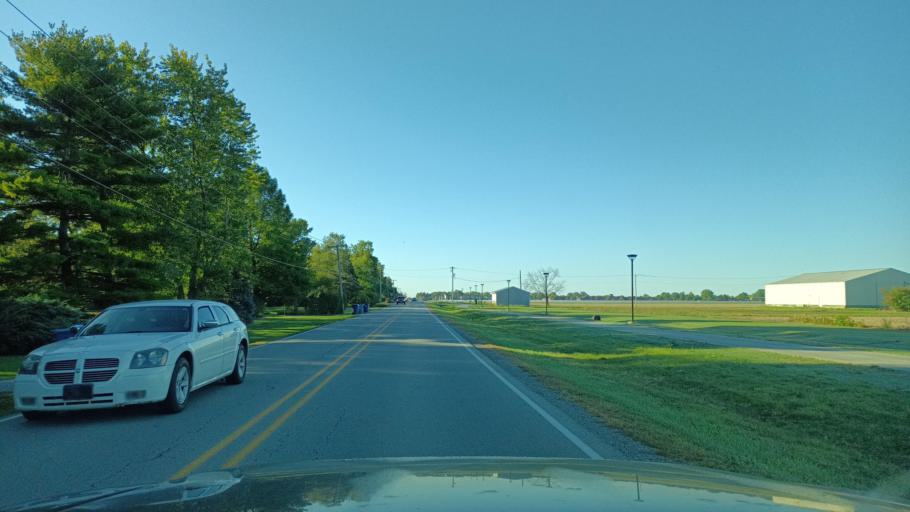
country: US
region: Illinois
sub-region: Champaign County
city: Savoy
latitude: 40.0779
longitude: -88.2385
